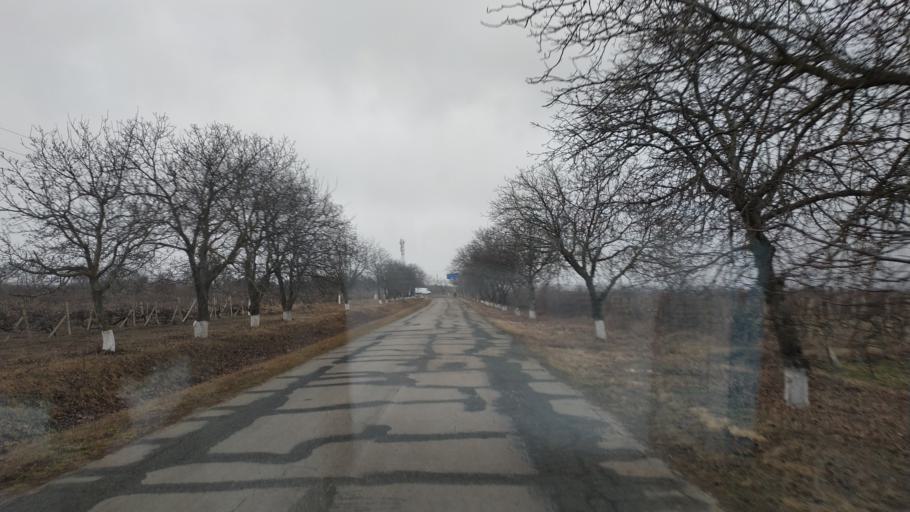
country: MD
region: Laloveni
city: Ialoveni
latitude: 46.8956
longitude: 28.6817
